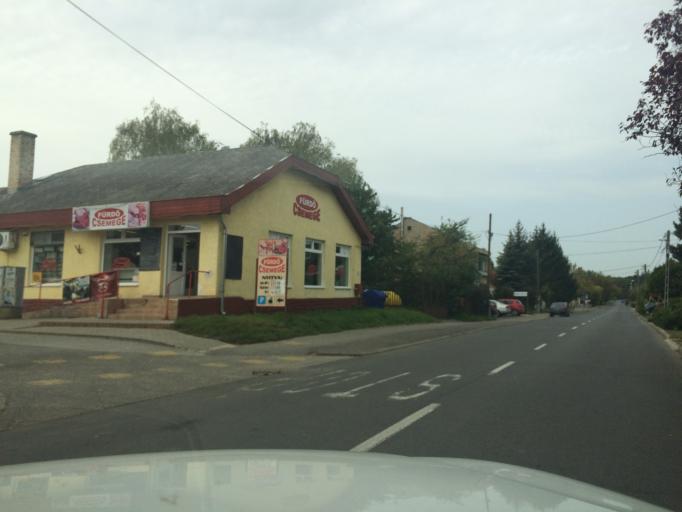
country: HU
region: Szabolcs-Szatmar-Bereg
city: Kotaj
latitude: 48.0087
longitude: 21.7372
